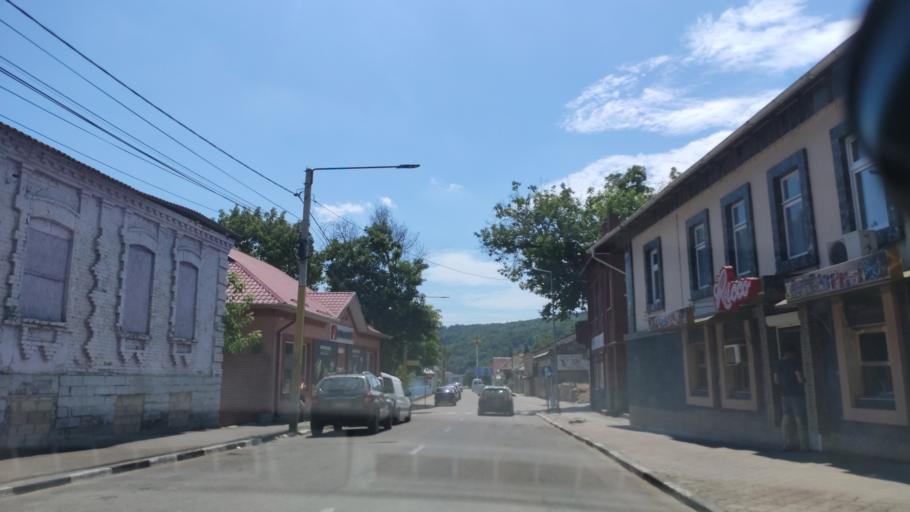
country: MD
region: Raionul Soroca
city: Soroca
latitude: 48.1593
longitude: 28.3002
